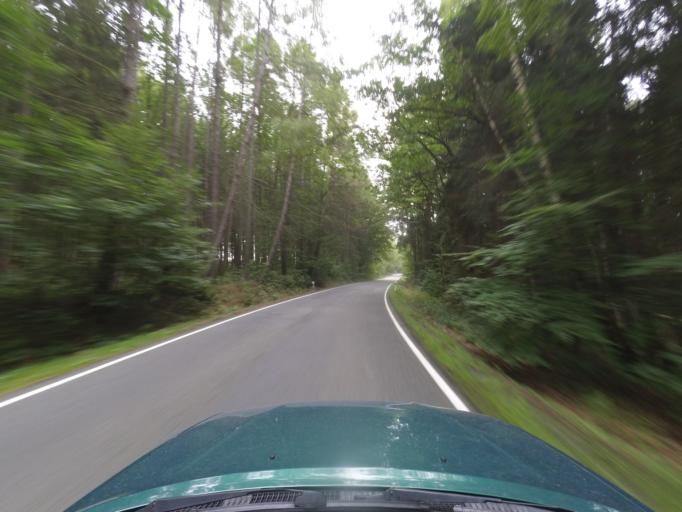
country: CZ
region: Plzensky
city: Bela nad Radbuzou
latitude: 49.5881
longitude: 12.6526
